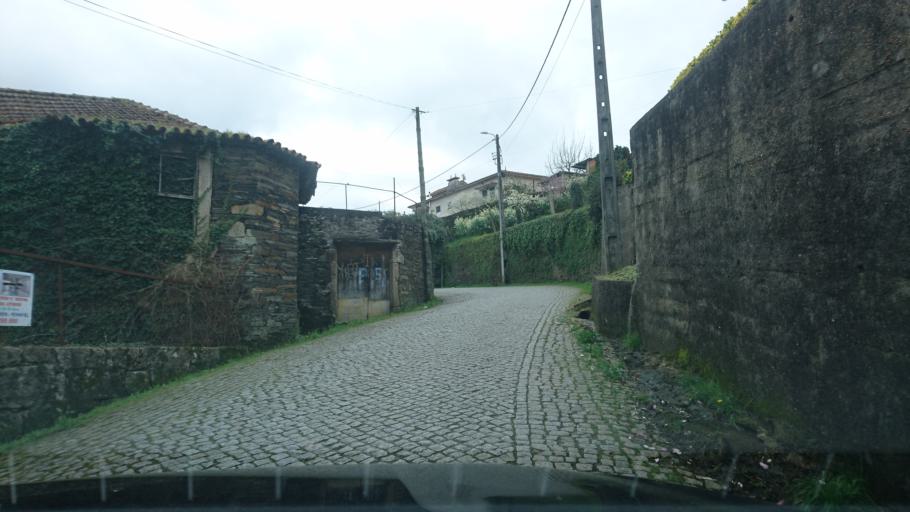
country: PT
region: Porto
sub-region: Paredes
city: Recarei
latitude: 41.1405
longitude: -8.3930
